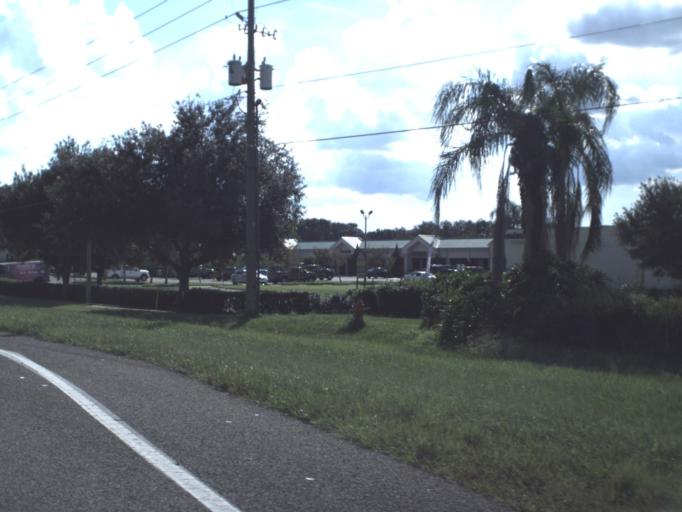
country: US
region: Florida
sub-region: Polk County
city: Medulla
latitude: 27.9447
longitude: -81.9730
